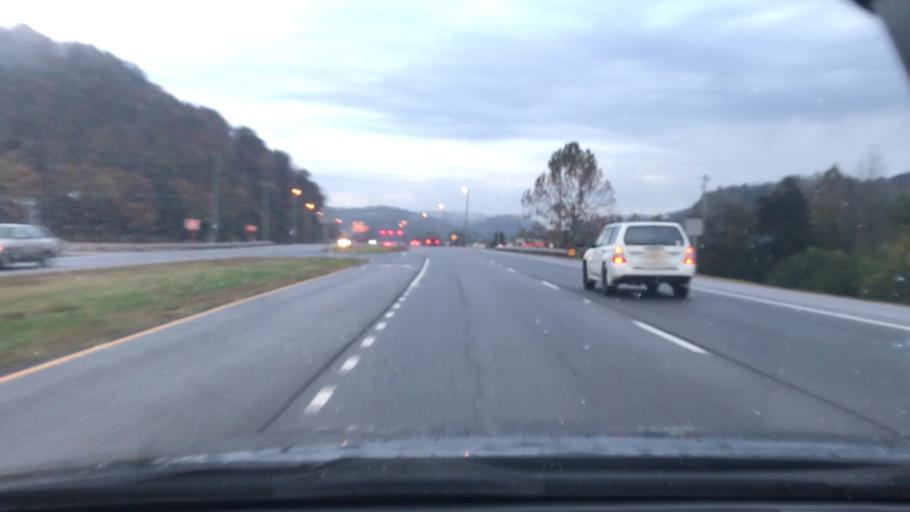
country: US
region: Tennessee
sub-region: Cheatham County
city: Ashland City
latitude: 36.2522
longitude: -87.0356
